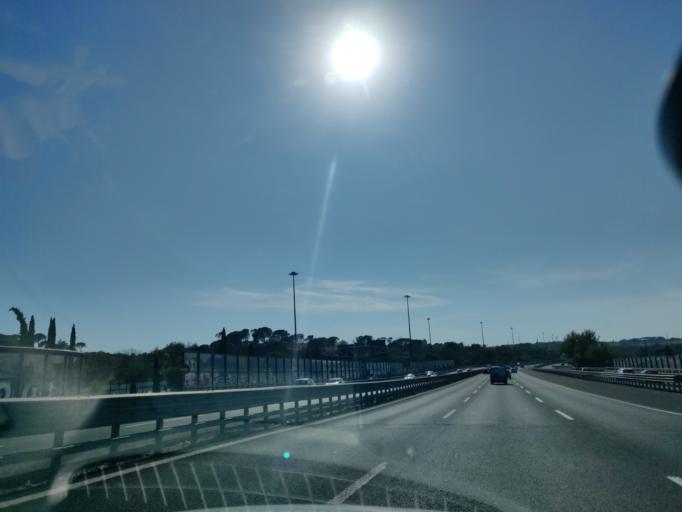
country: IT
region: Latium
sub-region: Citta metropolitana di Roma Capitale
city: Monte Caminetto
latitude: 41.9861
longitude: 12.4897
